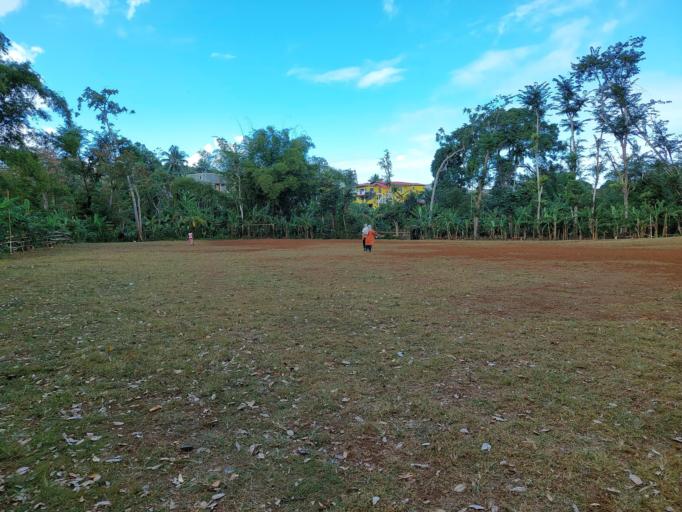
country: YT
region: Tsingoni
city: Tsingoni
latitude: -12.7861
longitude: 45.1084
